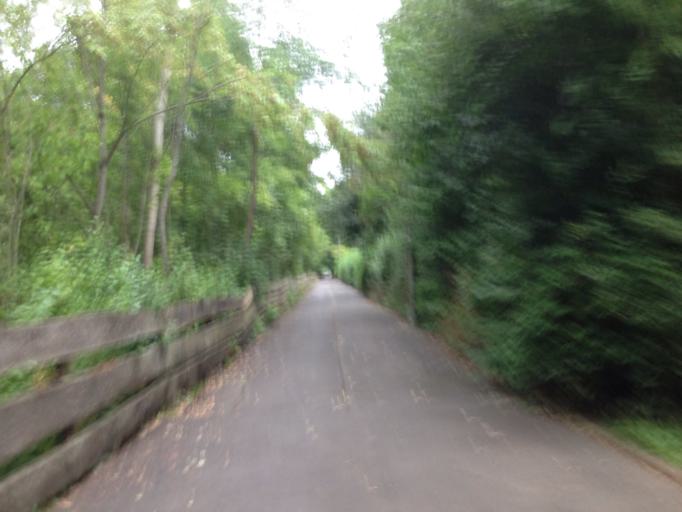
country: DE
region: Hesse
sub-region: Regierungsbezirk Giessen
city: Giessen
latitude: 50.5908
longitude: 8.6559
